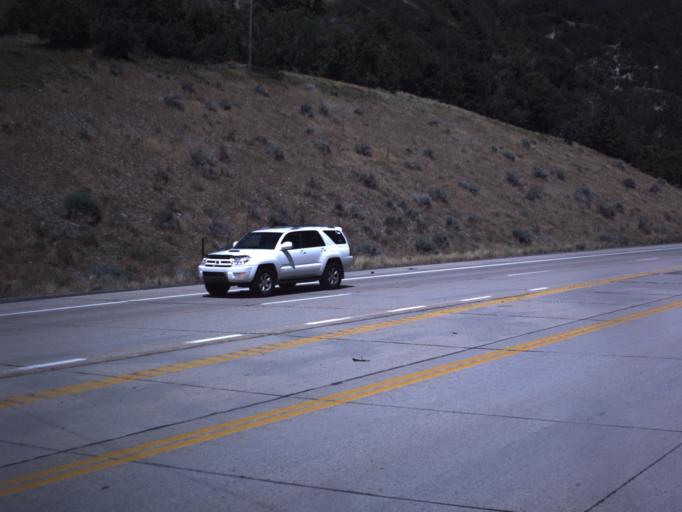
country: US
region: Utah
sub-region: Utah County
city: Orem
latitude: 40.3547
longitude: -111.5795
